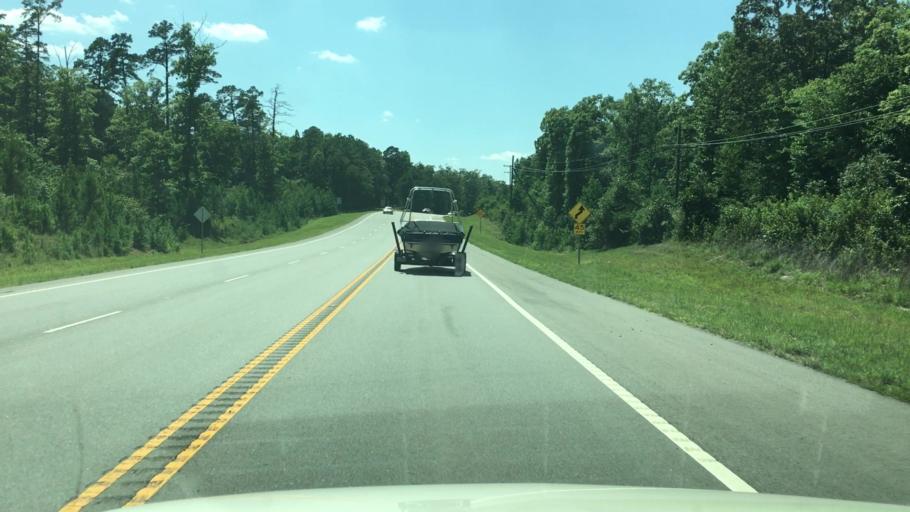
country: US
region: Arkansas
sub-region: Garland County
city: Piney
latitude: 34.5228
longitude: -93.3231
